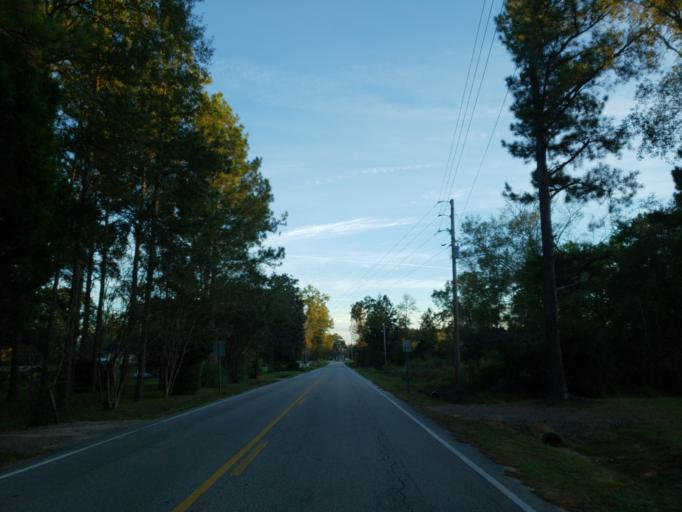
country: US
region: Mississippi
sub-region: Wayne County
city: Belmont
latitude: 31.4316
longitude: -88.4726
